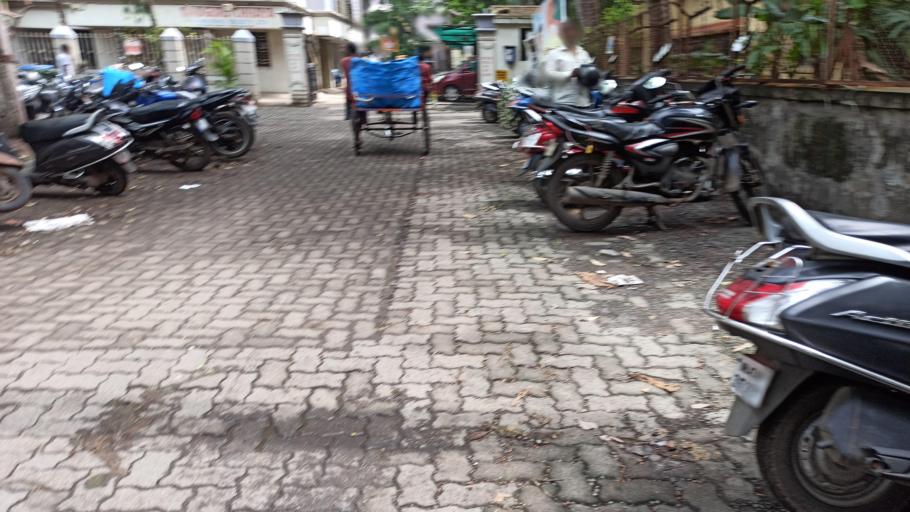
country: IN
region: Maharashtra
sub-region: Mumbai Suburban
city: Borivli
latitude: 19.2594
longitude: 72.8599
